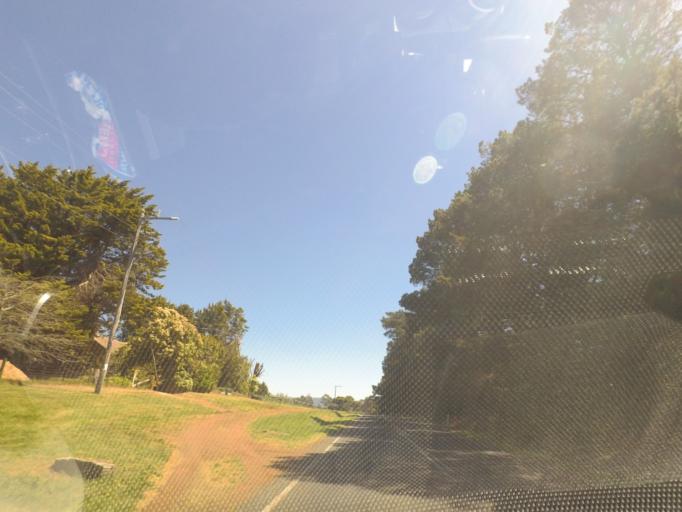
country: AU
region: Victoria
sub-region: Hume
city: Sunbury
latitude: -37.2788
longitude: 144.7470
